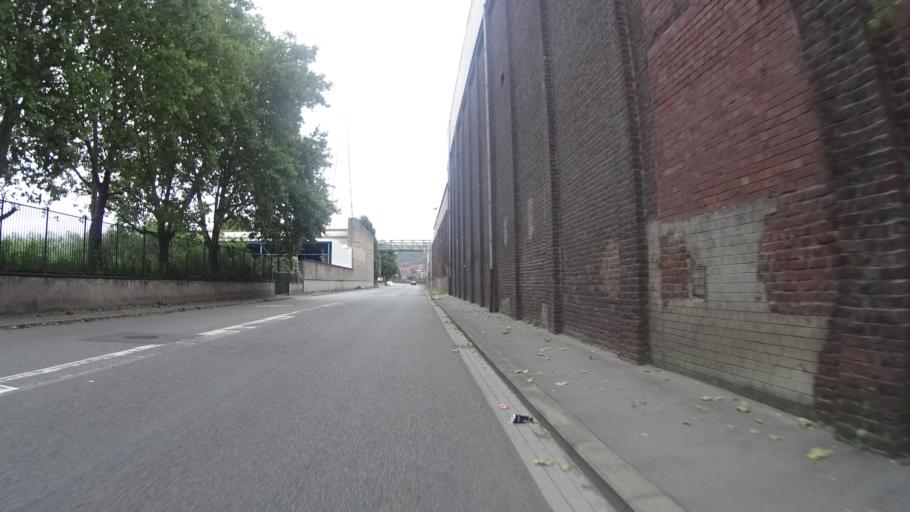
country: BE
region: Wallonia
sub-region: Province de Liege
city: Saint-Nicolas
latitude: 50.6154
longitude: 5.5320
